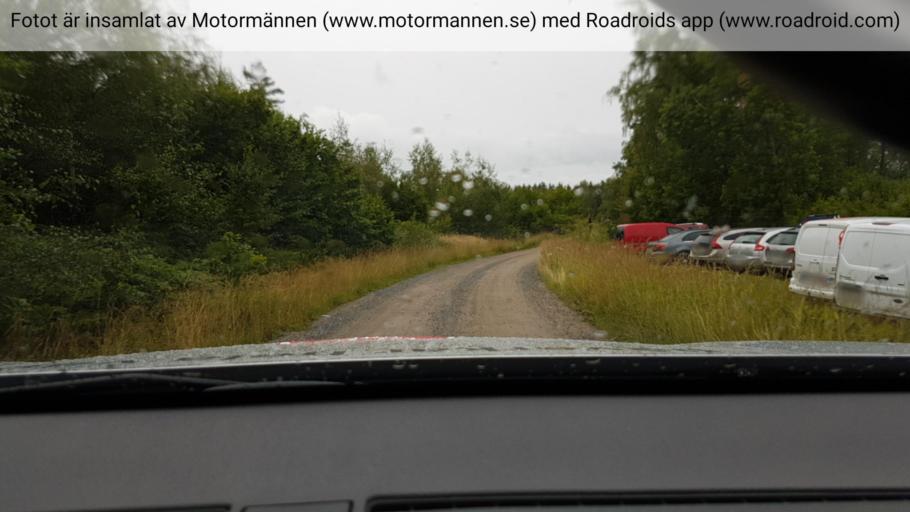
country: SE
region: Stockholm
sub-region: Nynashamns Kommun
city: Nynashamn
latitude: 58.9354
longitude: 17.9121
